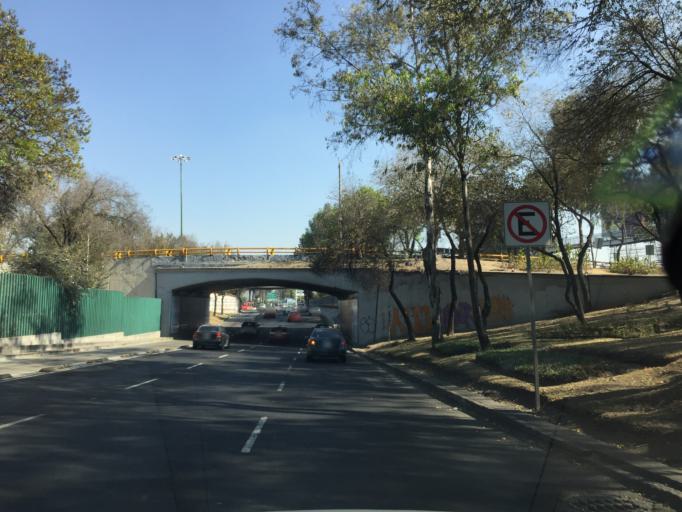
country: MX
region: Mexico City
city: Cuauhtemoc
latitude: 19.4650
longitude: -99.1416
